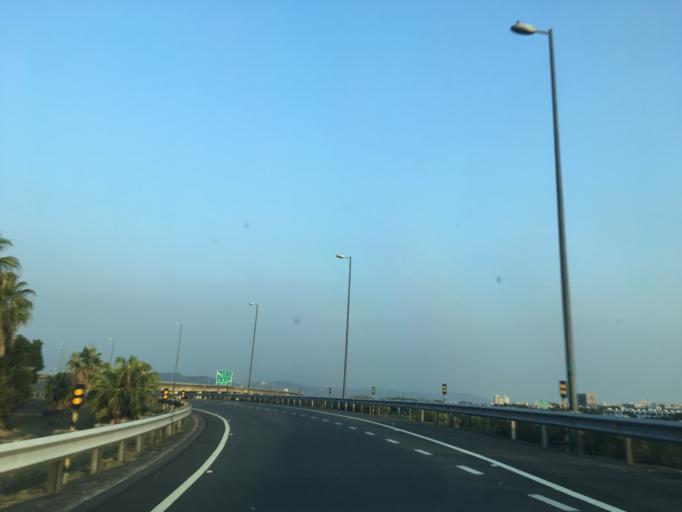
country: TW
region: Taiwan
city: Zhongxing New Village
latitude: 23.9476
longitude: 120.6676
